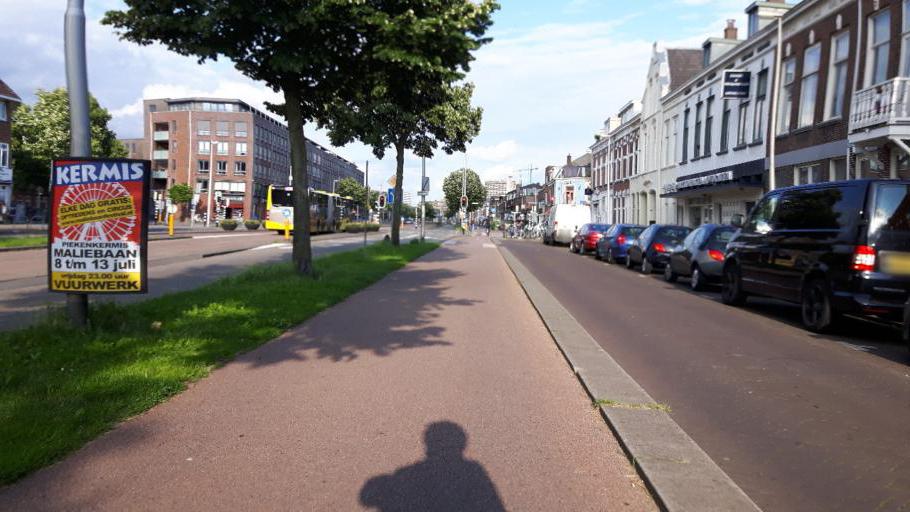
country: NL
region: Utrecht
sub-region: Gemeente Utrecht
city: Utrecht
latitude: 52.0935
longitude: 5.0954
